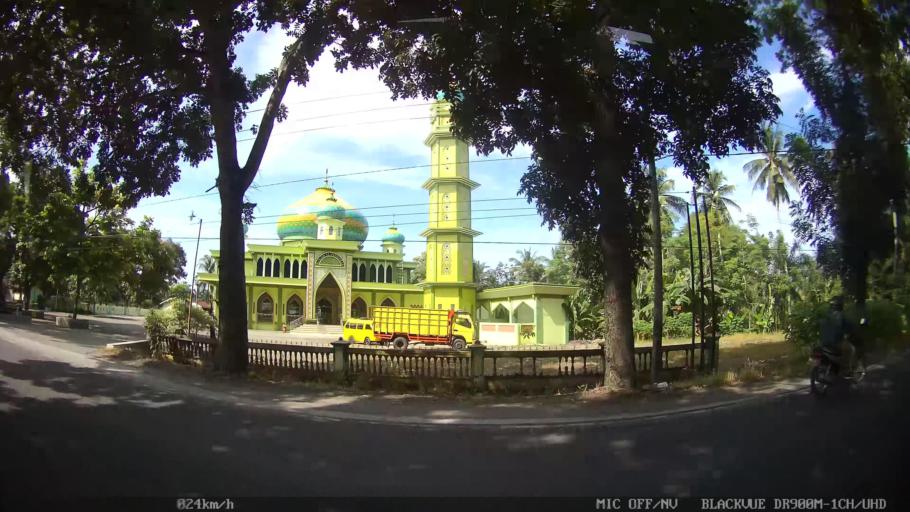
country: ID
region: North Sumatra
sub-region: Kabupaten Langkat
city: Stabat
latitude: 3.7296
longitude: 98.4949
